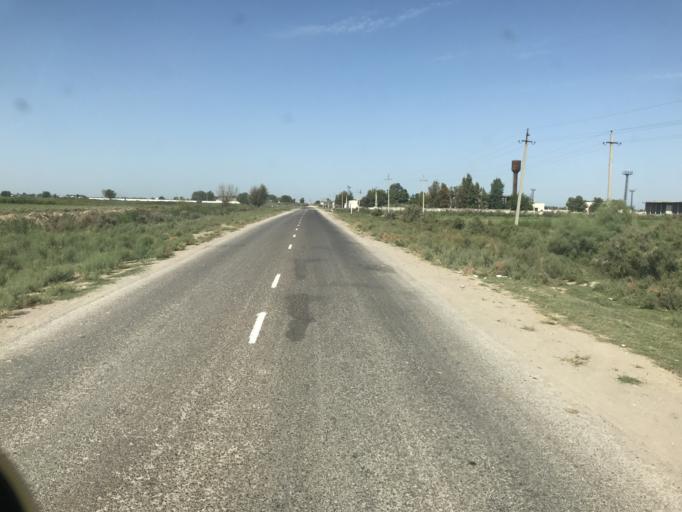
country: KZ
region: Ongtustik Qazaqstan
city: Myrzakent
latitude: 40.6855
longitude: 68.5663
